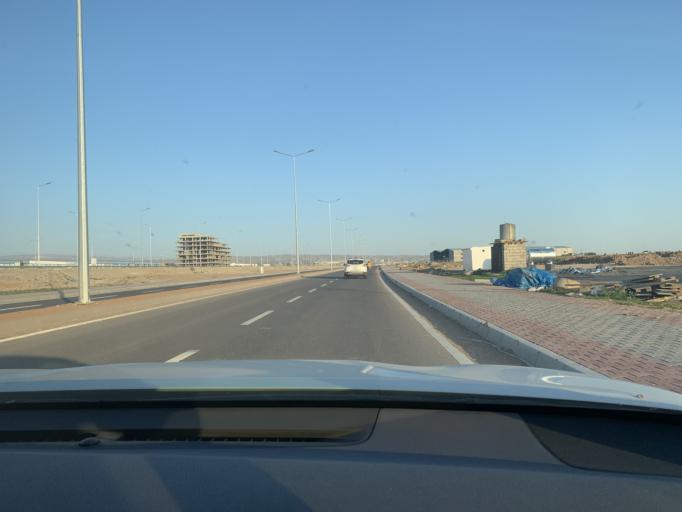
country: IQ
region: Arbil
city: Erbil
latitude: 36.2850
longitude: 44.0481
